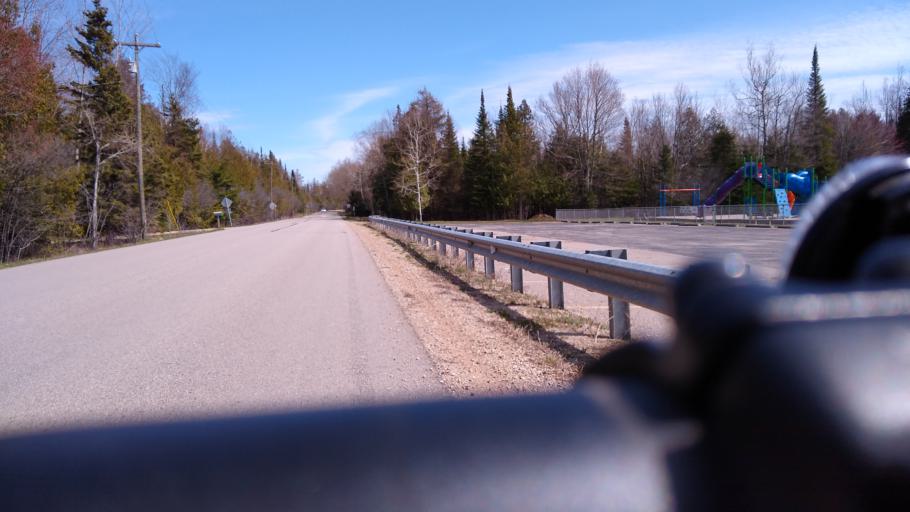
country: US
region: Michigan
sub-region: Delta County
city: Escanaba
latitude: 45.6860
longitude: -87.1512
